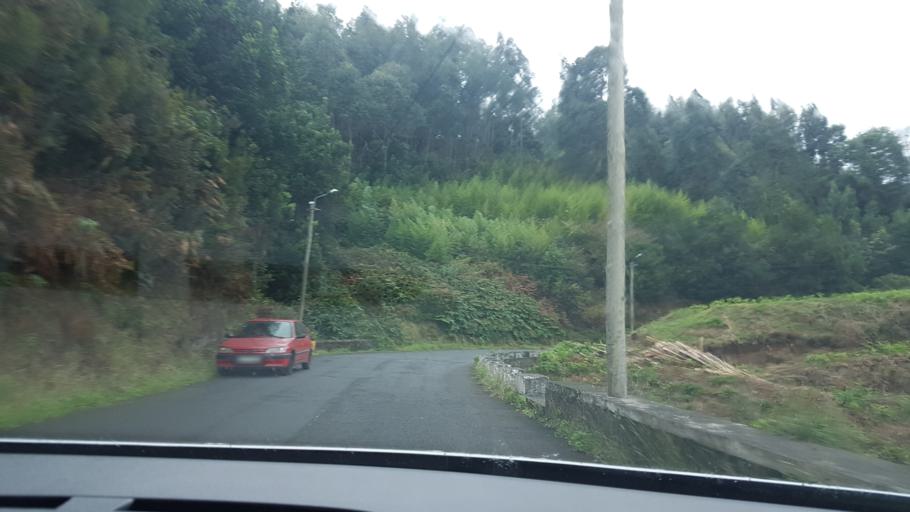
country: PT
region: Madeira
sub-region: Santa Cruz
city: Santa Cruz
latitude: 32.7306
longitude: -16.8103
